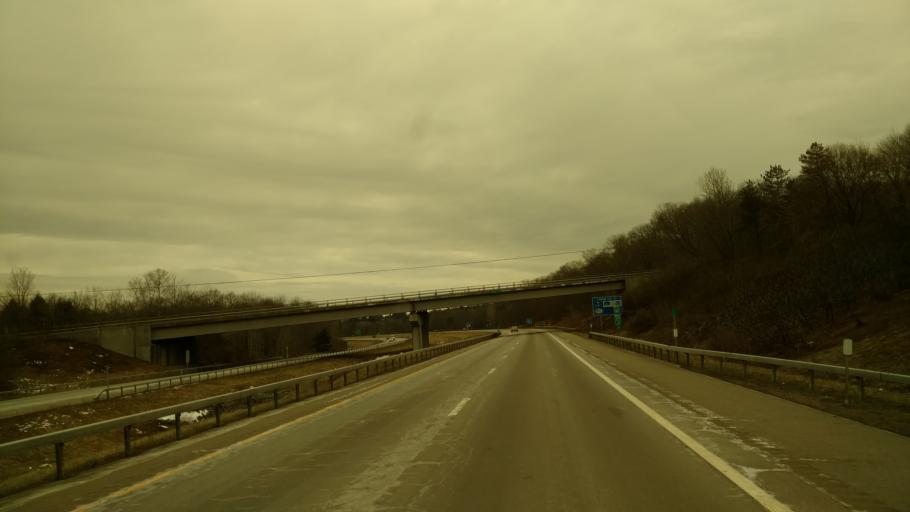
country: US
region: New York
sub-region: Chautauqua County
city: Falconer
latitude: 42.1249
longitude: -79.2226
